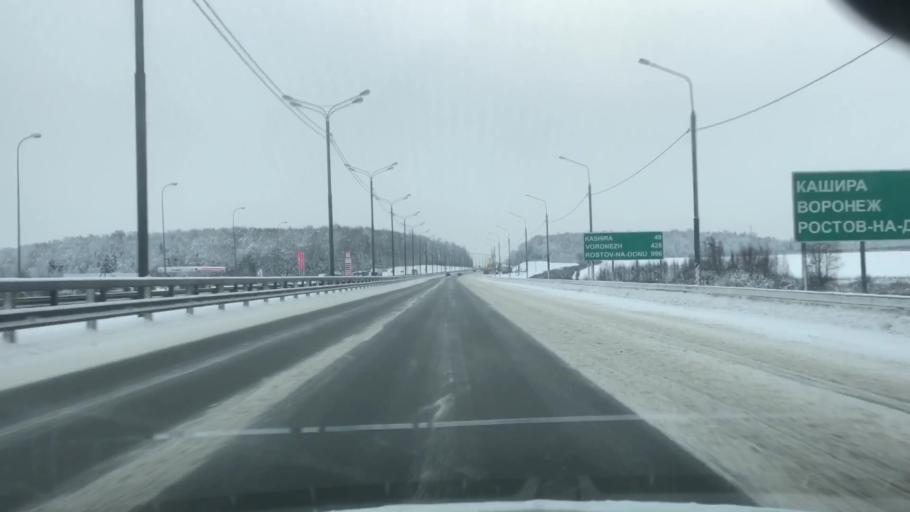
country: RU
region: Moskovskaya
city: Mikhnevo
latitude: 55.1842
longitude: 37.9021
